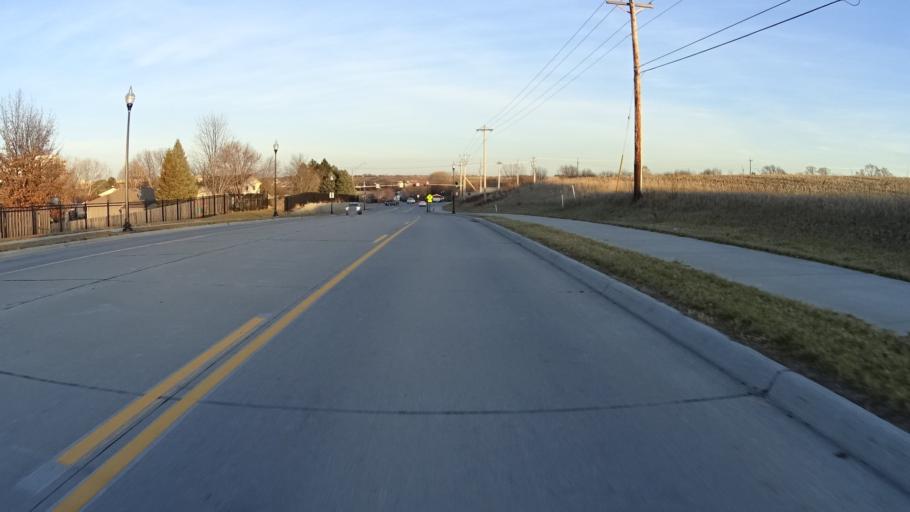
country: US
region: Nebraska
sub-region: Sarpy County
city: Papillion
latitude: 41.1326
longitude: -96.0450
